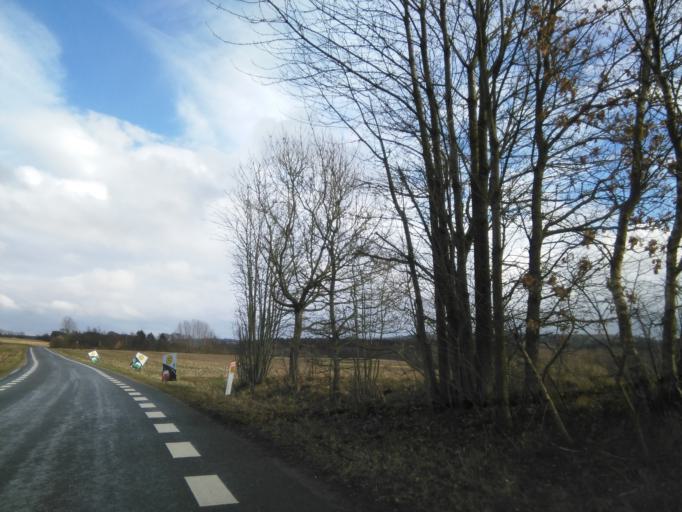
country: DK
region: Central Jutland
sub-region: Skanderborg Kommune
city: Ry
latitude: 56.1089
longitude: 9.8011
